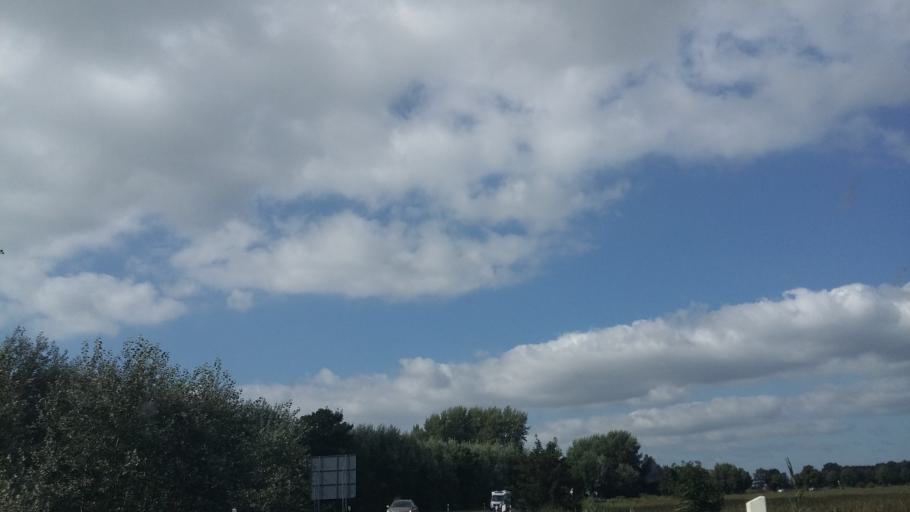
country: DE
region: Lower Saxony
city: Loxstedt
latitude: 53.4696
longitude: 8.5974
